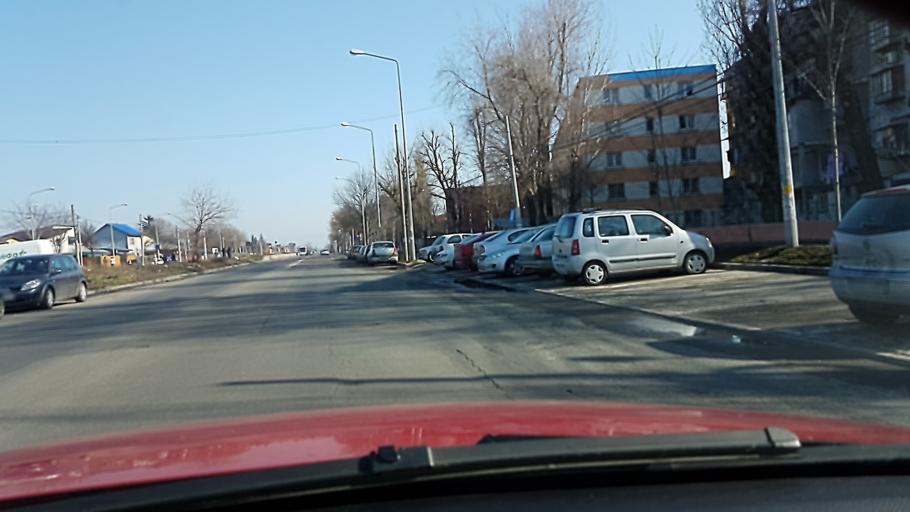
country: RO
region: Ilfov
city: Dobroesti
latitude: 44.4326
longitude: 26.1903
